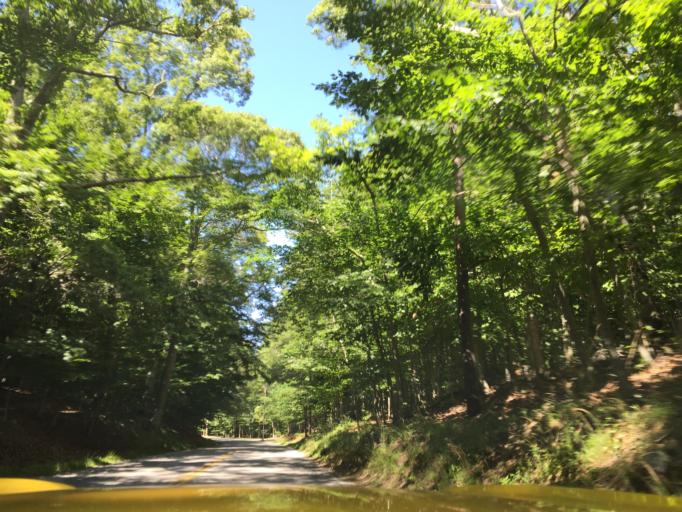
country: US
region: New York
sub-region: Suffolk County
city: Amagansett
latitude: 40.9895
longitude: -72.1347
